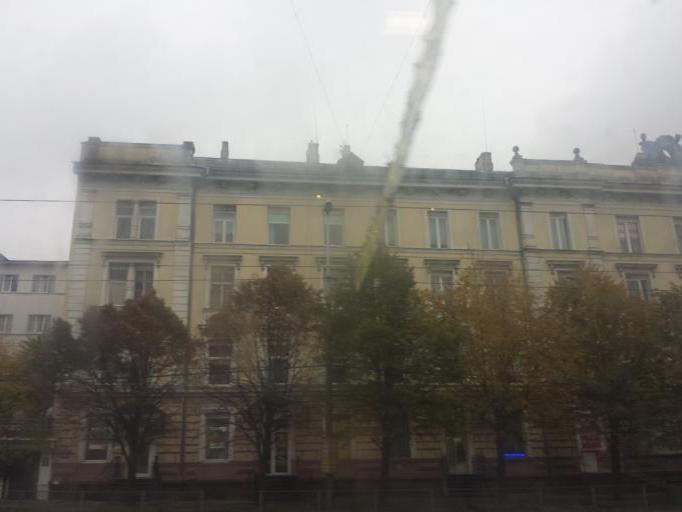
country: RU
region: Kaliningrad
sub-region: Gorod Kaliningrad
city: Kaliningrad
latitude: 54.7010
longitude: 20.5040
